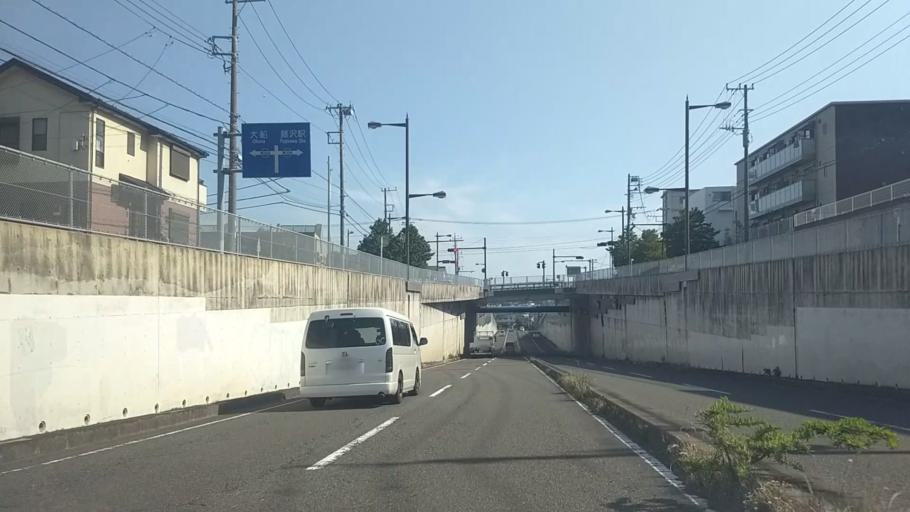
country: JP
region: Kanagawa
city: Fujisawa
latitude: 35.3502
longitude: 139.5007
